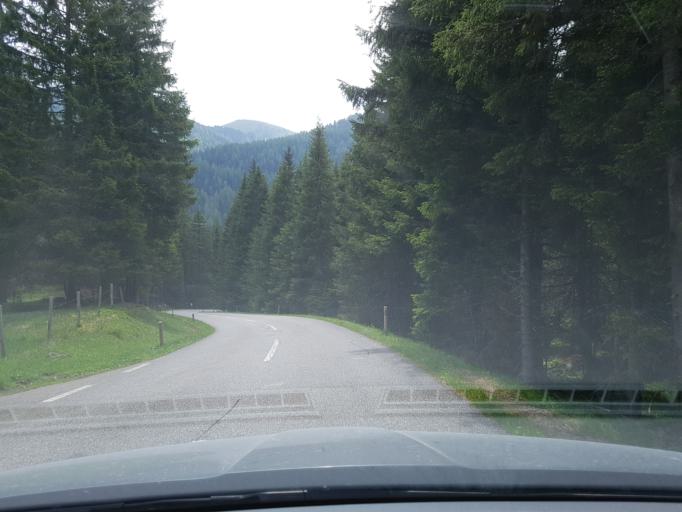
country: AT
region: Carinthia
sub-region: Politischer Bezirk Spittal an der Drau
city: Kleinkirchheim
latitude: 46.8941
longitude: 13.8217
